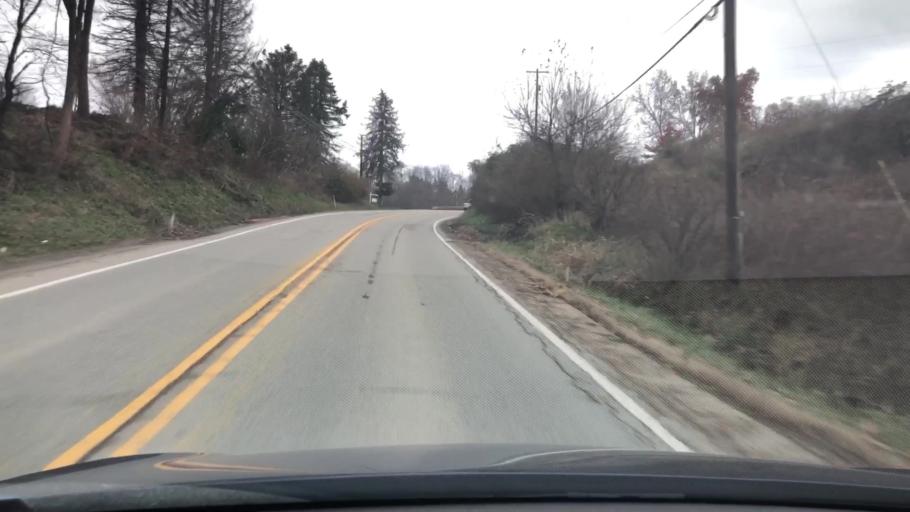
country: US
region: Pennsylvania
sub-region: Armstrong County
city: Kittanning
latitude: 40.8428
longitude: -79.4639
